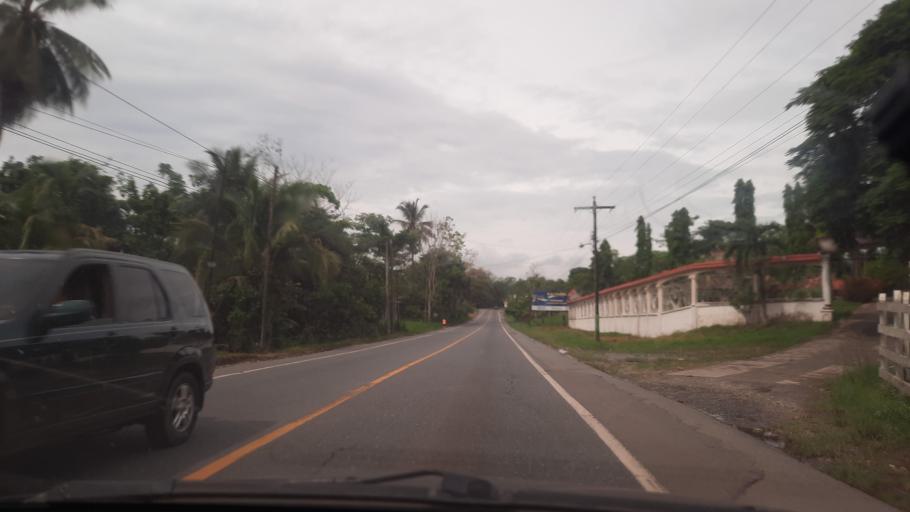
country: GT
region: Izabal
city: Morales
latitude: 15.5184
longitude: -88.7979
